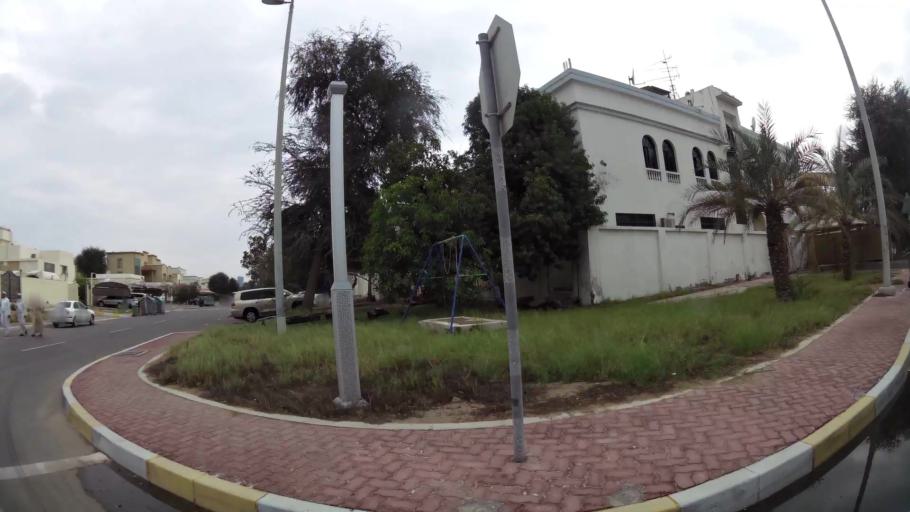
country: AE
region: Abu Dhabi
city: Abu Dhabi
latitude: 24.4353
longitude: 54.4004
